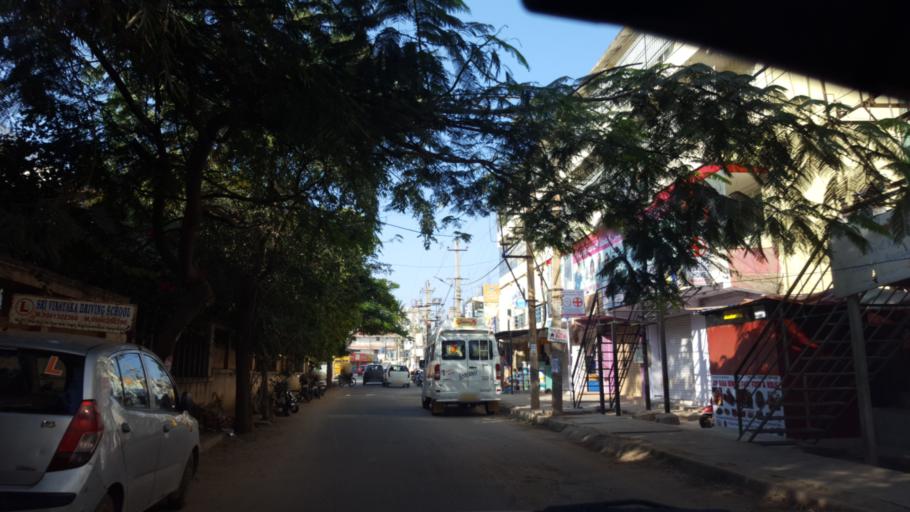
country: IN
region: Karnataka
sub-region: Bangalore Urban
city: Bangalore
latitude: 12.9547
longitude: 77.7148
